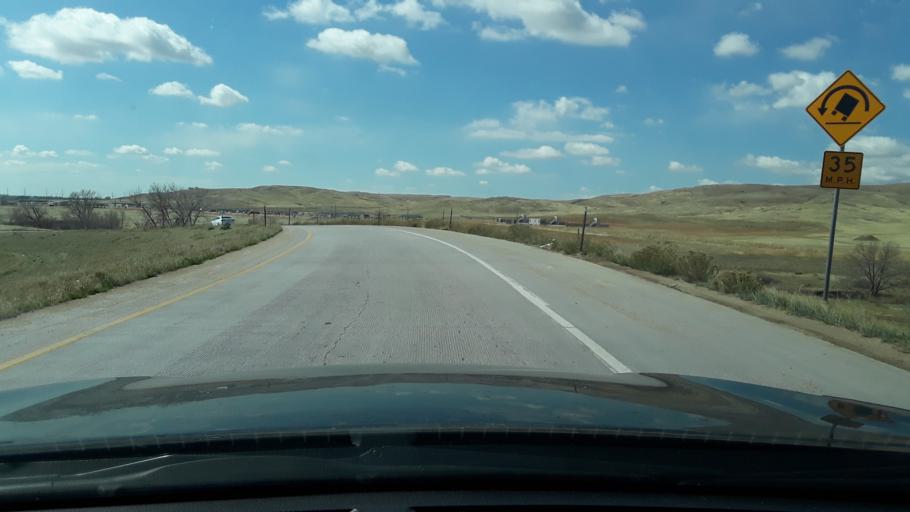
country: US
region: Colorado
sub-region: El Paso County
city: Security-Widefield
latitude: 38.7239
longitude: -104.7353
